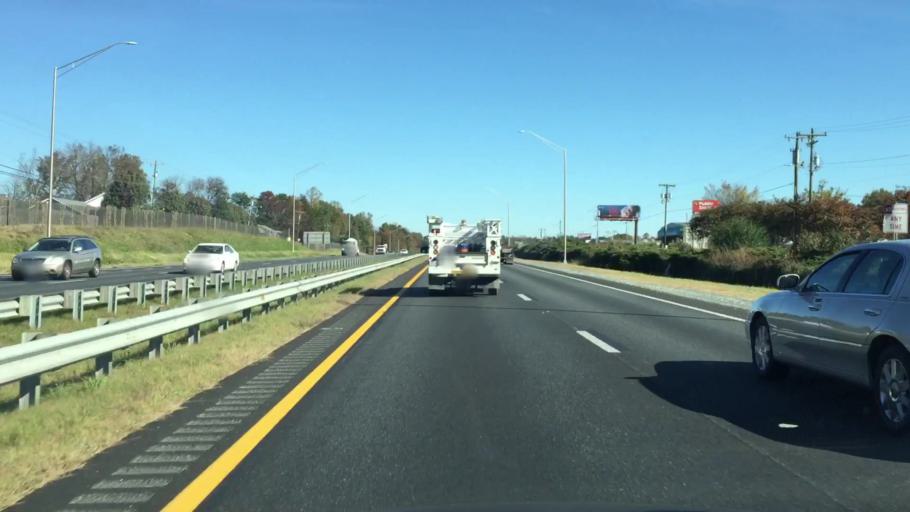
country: US
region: North Carolina
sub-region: Guilford County
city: Greensboro
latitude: 36.1188
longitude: -79.7528
